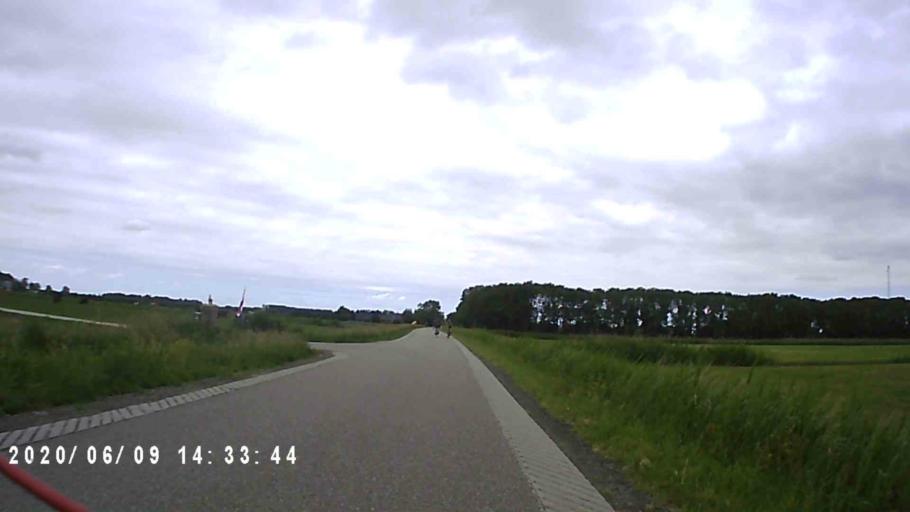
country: NL
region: Groningen
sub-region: Gemeente Bedum
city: Bedum
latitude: 53.3240
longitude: 6.5905
